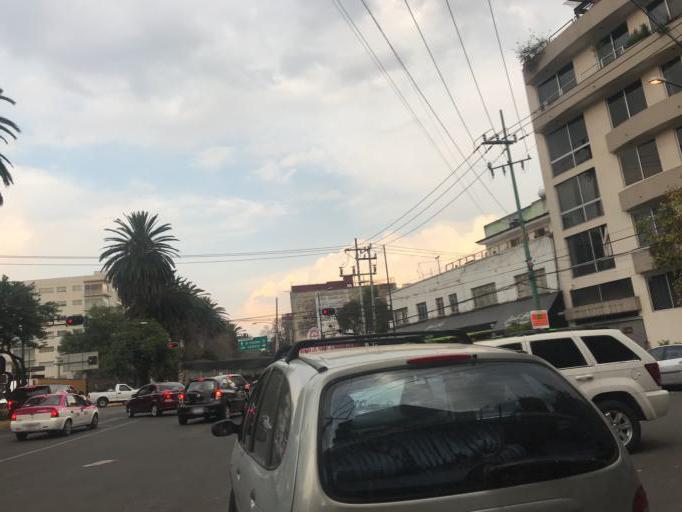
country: MX
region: Mexico City
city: Colonia del Valle
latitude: 19.3806
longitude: -99.1581
